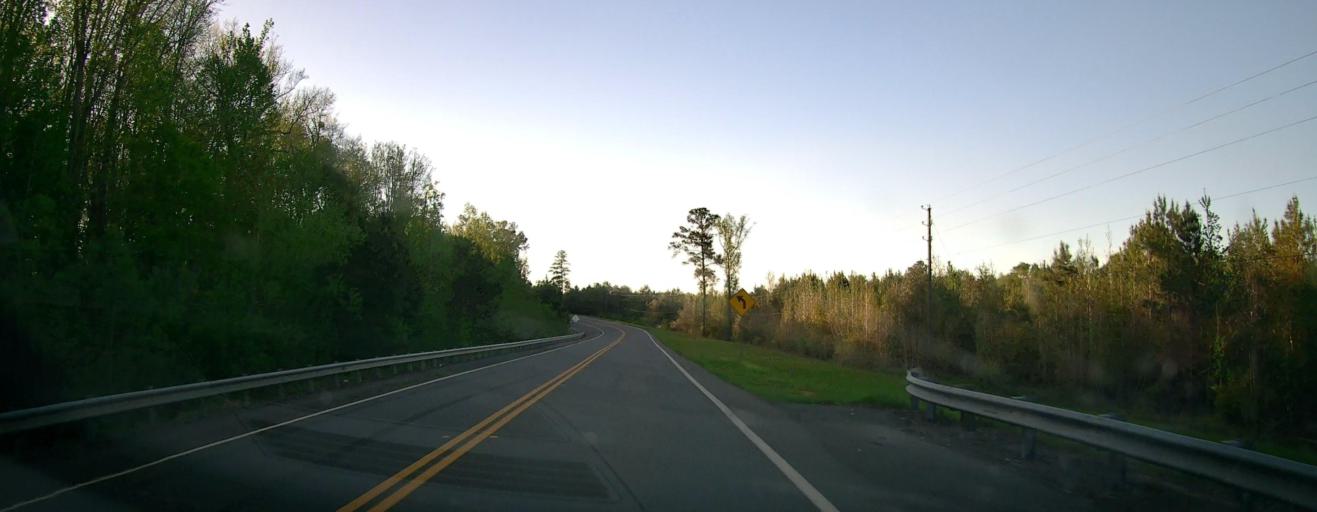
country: US
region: Georgia
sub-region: Macon County
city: Oglethorpe
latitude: 32.3098
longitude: -84.1621
